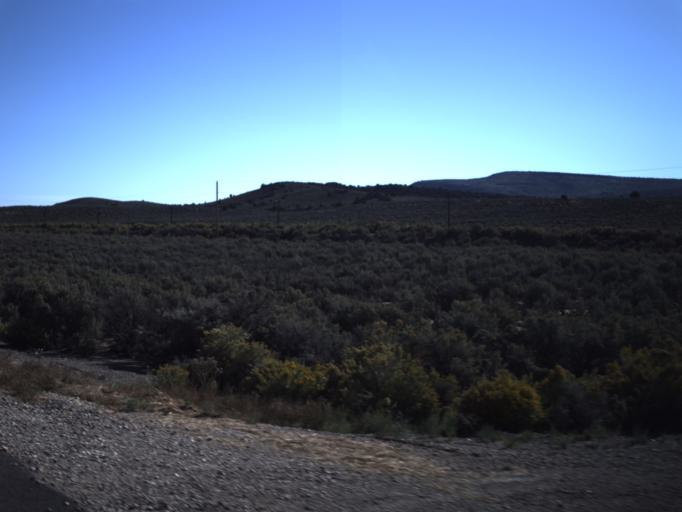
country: US
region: Utah
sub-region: Washington County
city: Enterprise
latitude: 37.7628
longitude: -113.9858
